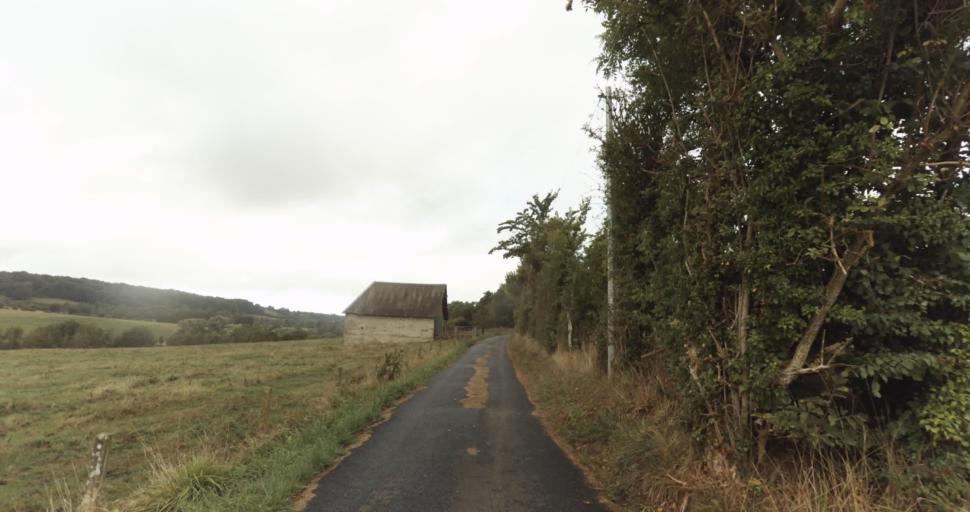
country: FR
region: Lower Normandy
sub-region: Departement de l'Orne
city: Vimoutiers
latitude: 48.8979
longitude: 0.2755
